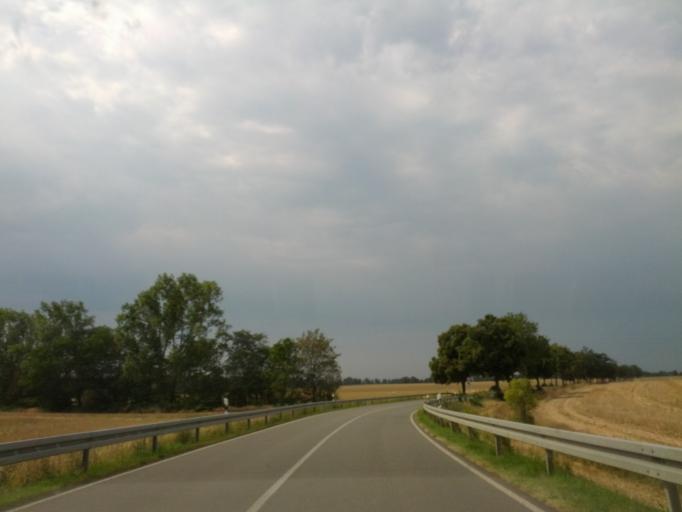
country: DE
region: Brandenburg
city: Fehrbellin
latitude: 52.7670
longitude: 12.8500
